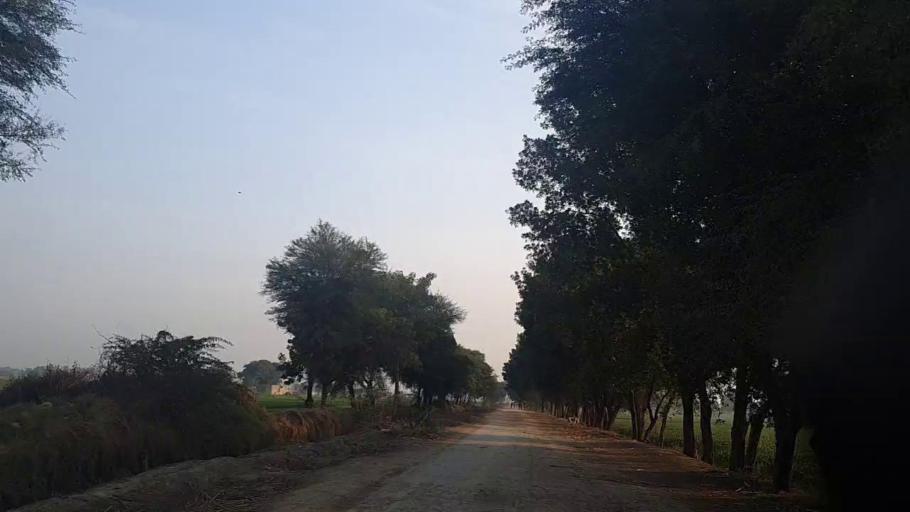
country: PK
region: Sindh
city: Sakrand
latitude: 26.1209
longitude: 68.2314
